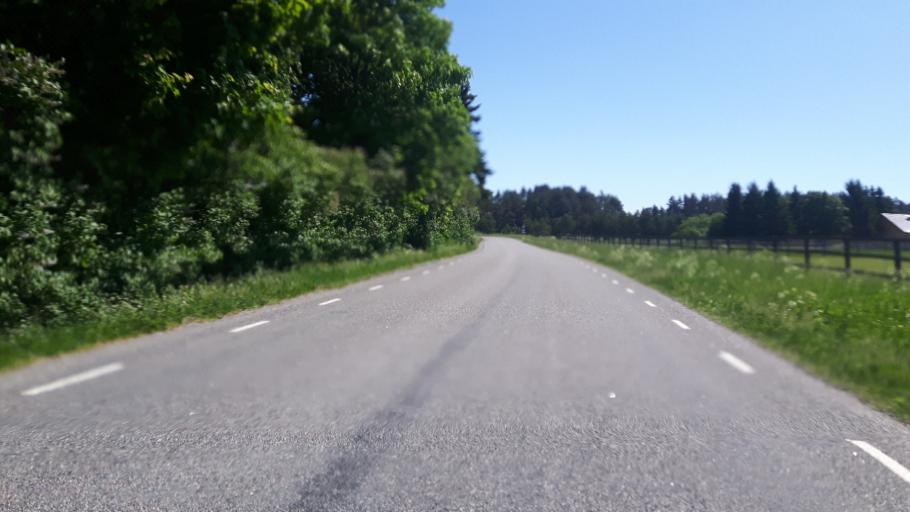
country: EE
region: Raplamaa
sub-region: Kohila vald
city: Kohila
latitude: 59.1952
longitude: 24.6988
